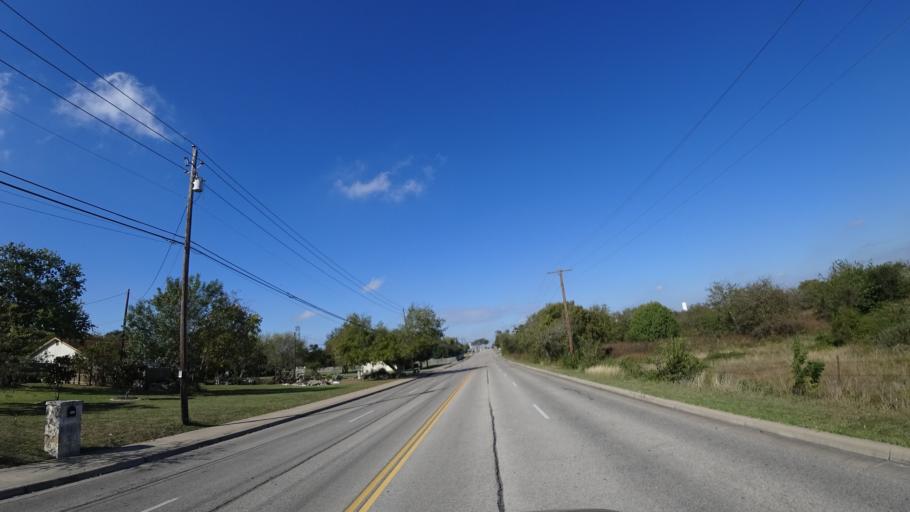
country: US
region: Texas
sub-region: Travis County
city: Windemere
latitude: 30.4442
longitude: -97.6462
